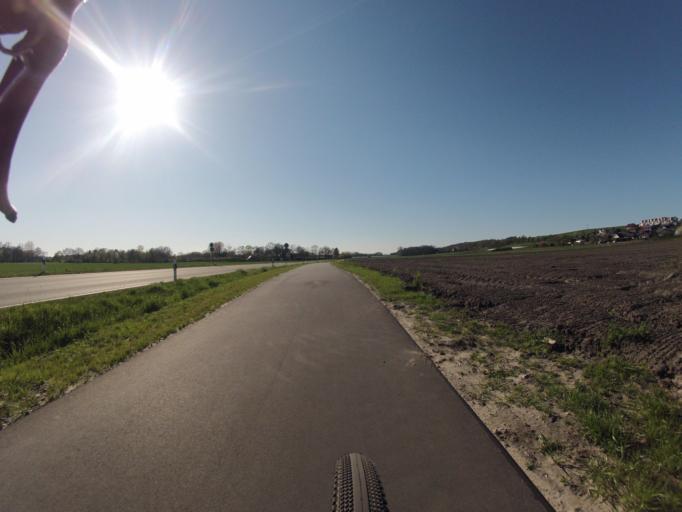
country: DE
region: North Rhine-Westphalia
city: Ibbenburen
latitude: 52.2222
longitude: 7.7366
